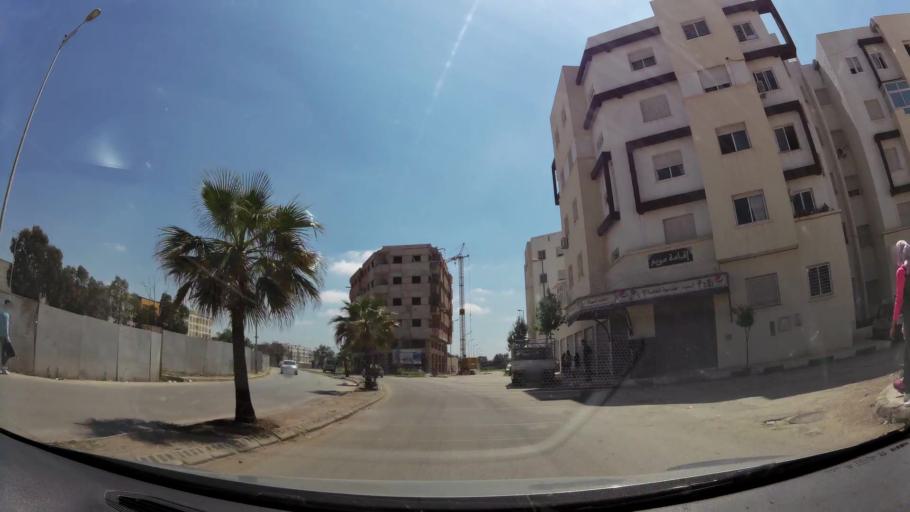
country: MA
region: Fes-Boulemane
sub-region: Fes
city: Fes
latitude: 34.0225
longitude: -5.0403
